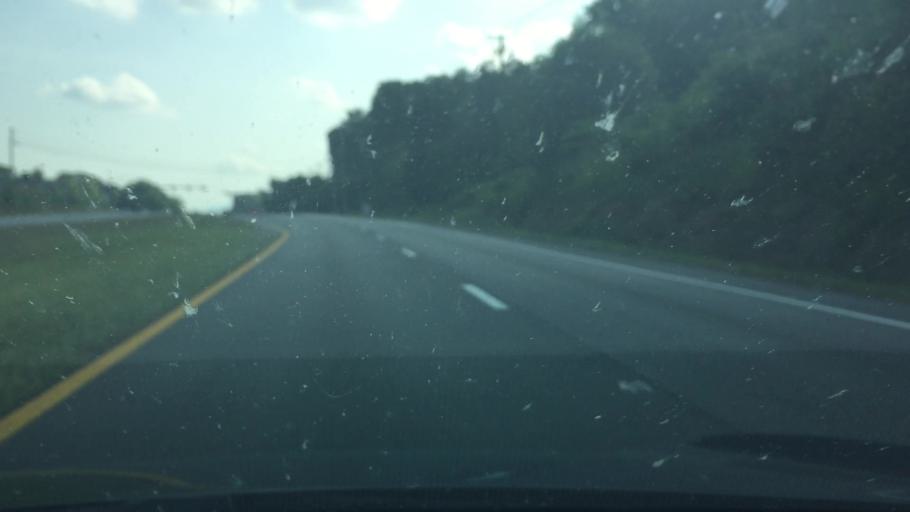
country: US
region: Virginia
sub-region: Roanoke County
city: Vinton
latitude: 37.3149
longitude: -79.8817
